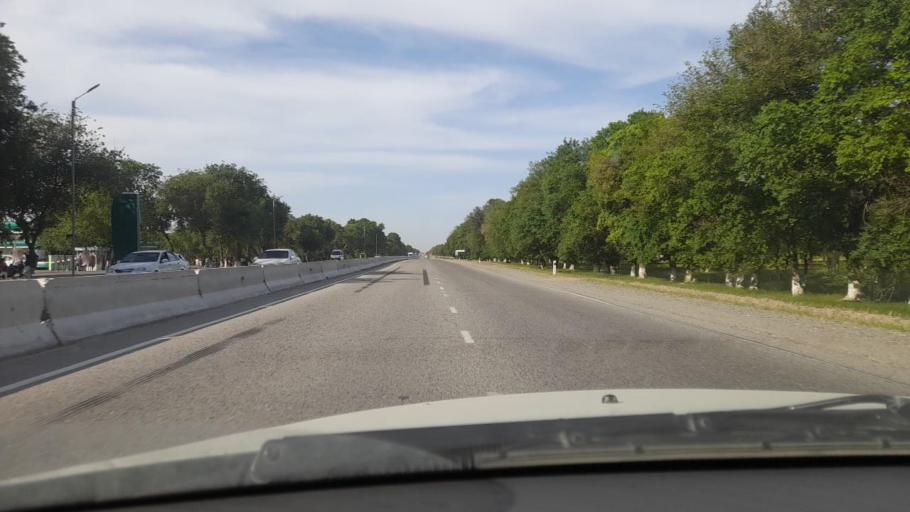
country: UZ
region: Samarqand
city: Bulung'ur
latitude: 39.8946
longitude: 67.4965
